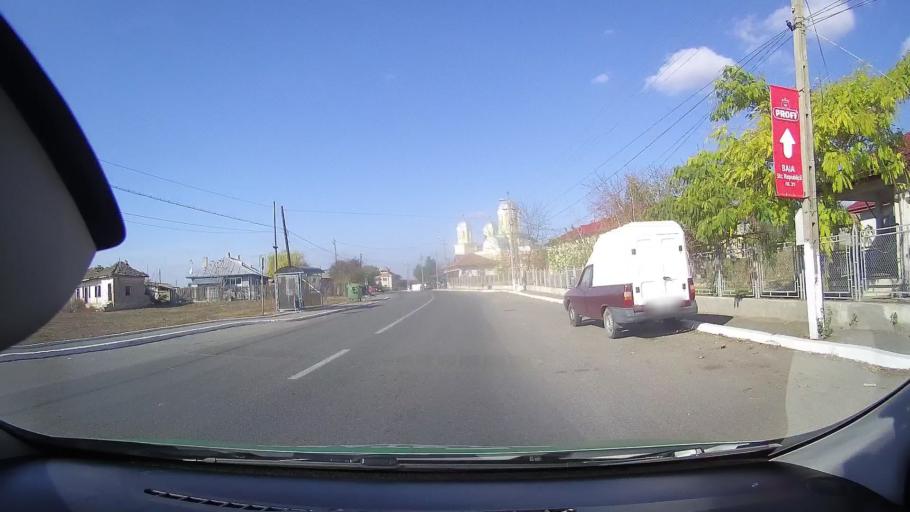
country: RO
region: Tulcea
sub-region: Comuna Ceamurlia de Jos
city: Ceamurlia de Jos
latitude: 44.7425
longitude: 28.7244
